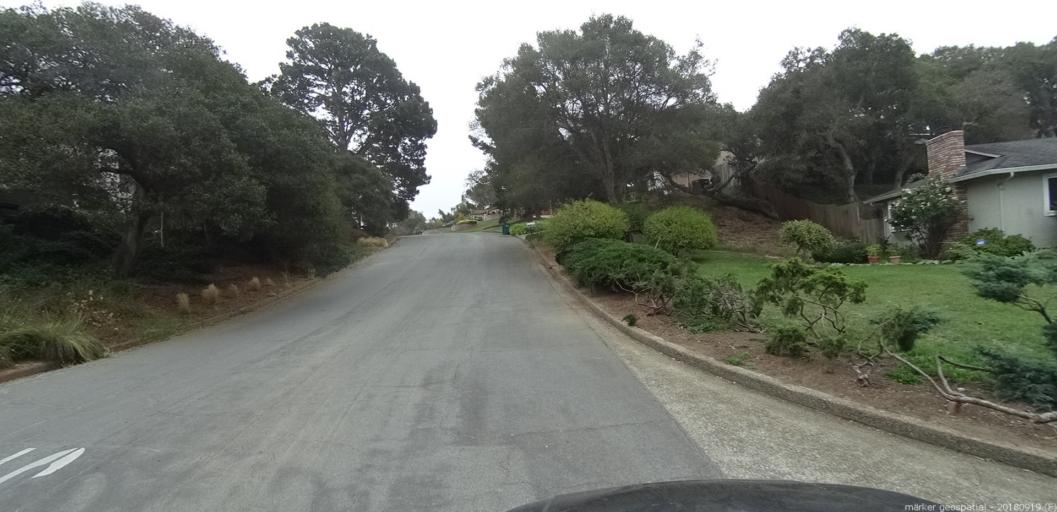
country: US
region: California
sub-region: Monterey County
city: Prunedale
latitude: 36.7801
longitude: -121.7120
